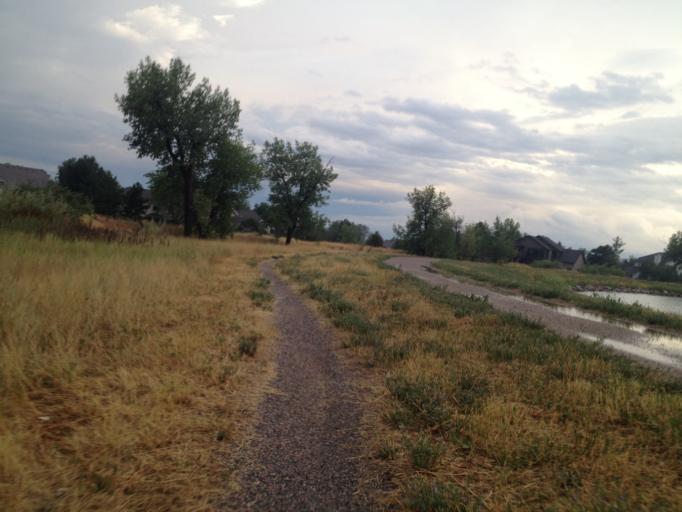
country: US
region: Colorado
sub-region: Boulder County
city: Louisville
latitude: 39.9804
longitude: -105.1604
